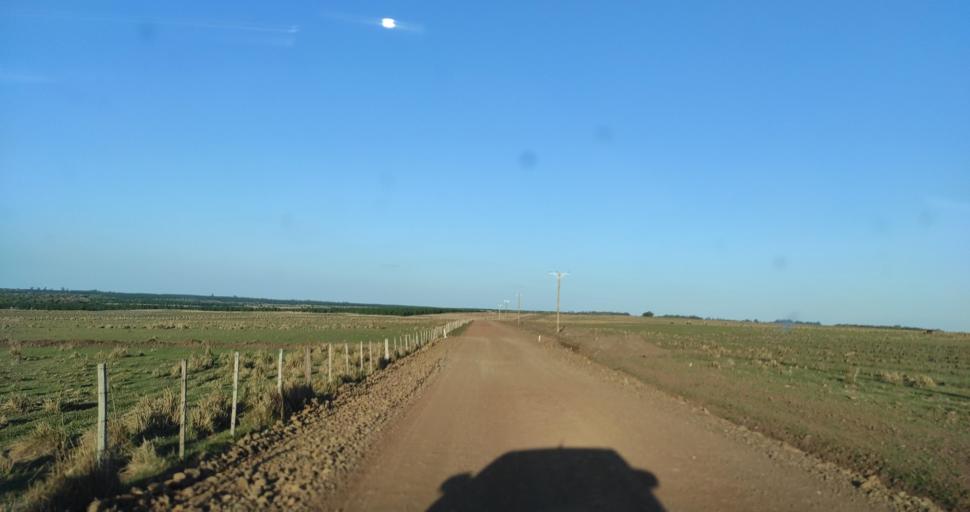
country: PY
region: Itapua
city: Carmen del Parana
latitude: -27.4114
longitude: -56.1476
